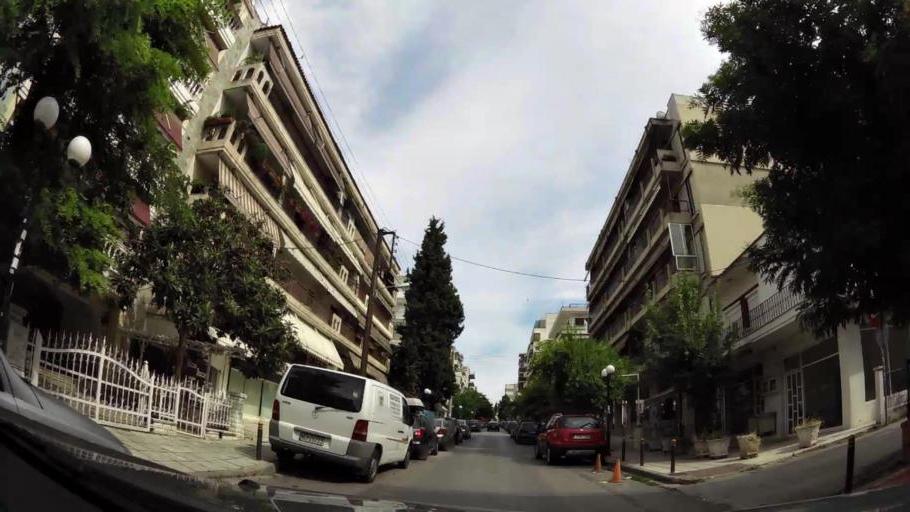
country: GR
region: Central Macedonia
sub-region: Nomos Thessalonikis
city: Kalamaria
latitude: 40.5859
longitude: 22.9502
